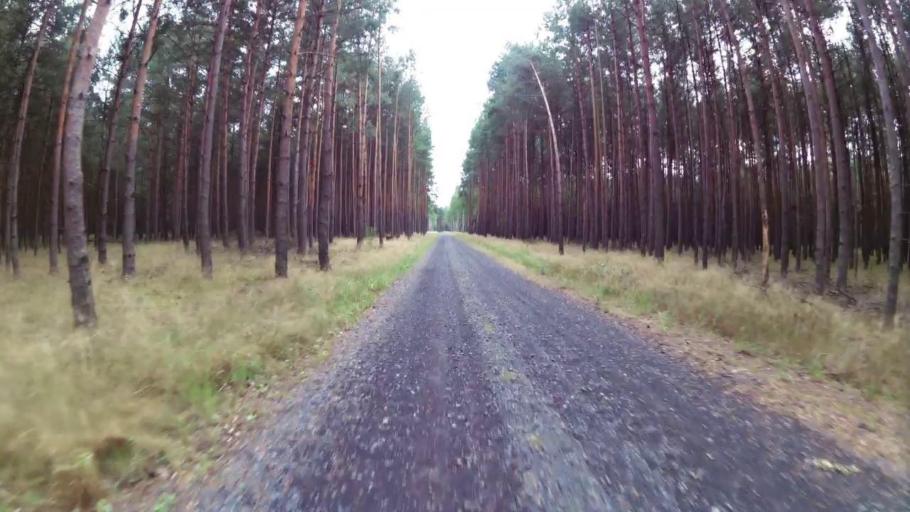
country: PL
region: West Pomeranian Voivodeship
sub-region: Powiat mysliborski
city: Debno
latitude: 52.7851
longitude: 14.7211
